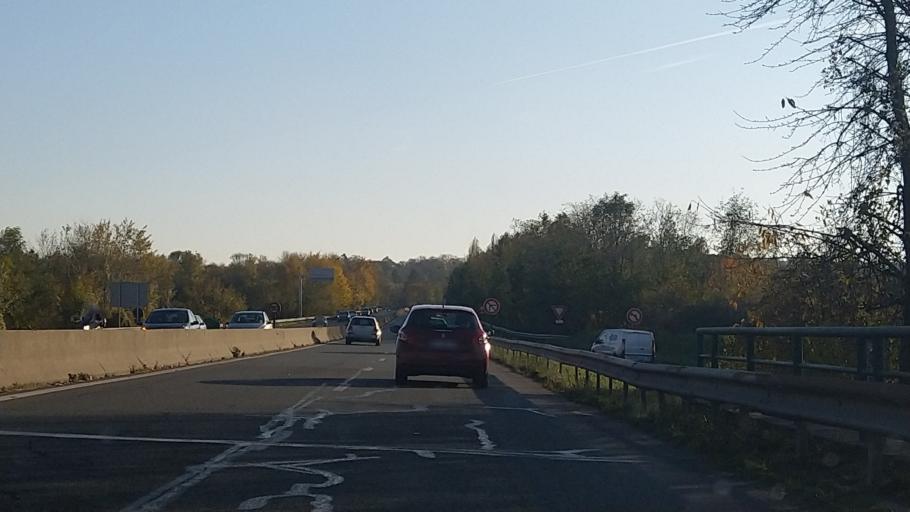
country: FR
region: Ile-de-France
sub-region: Departement du Val-d'Oise
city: Moisselles
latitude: 49.0343
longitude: 2.3459
